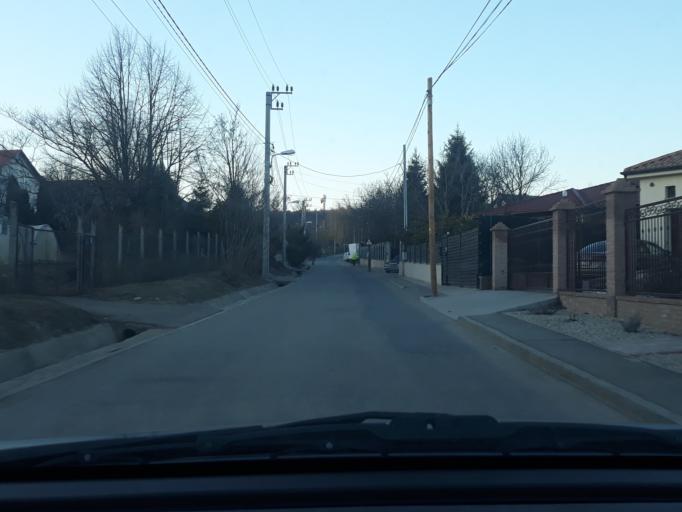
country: RO
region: Bihor
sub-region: Comuna Biharea
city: Oradea
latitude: 47.0836
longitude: 21.9466
